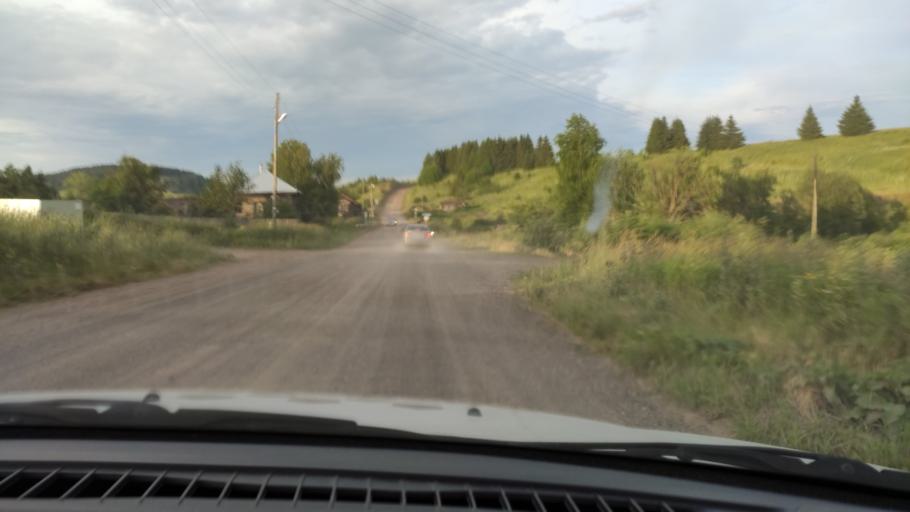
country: RU
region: Perm
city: Kukushtan
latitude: 57.4362
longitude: 56.3360
